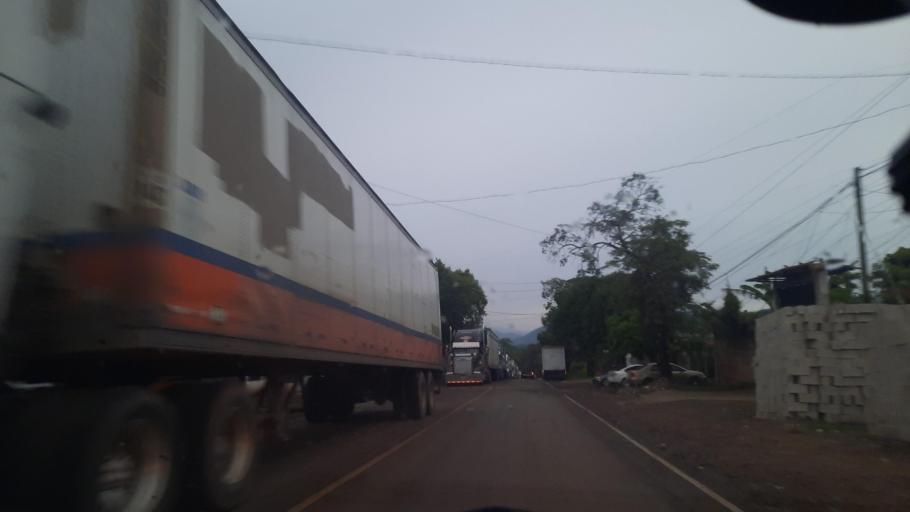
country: GT
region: Jutiapa
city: Atescatempa
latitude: 14.1914
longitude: -89.6711
